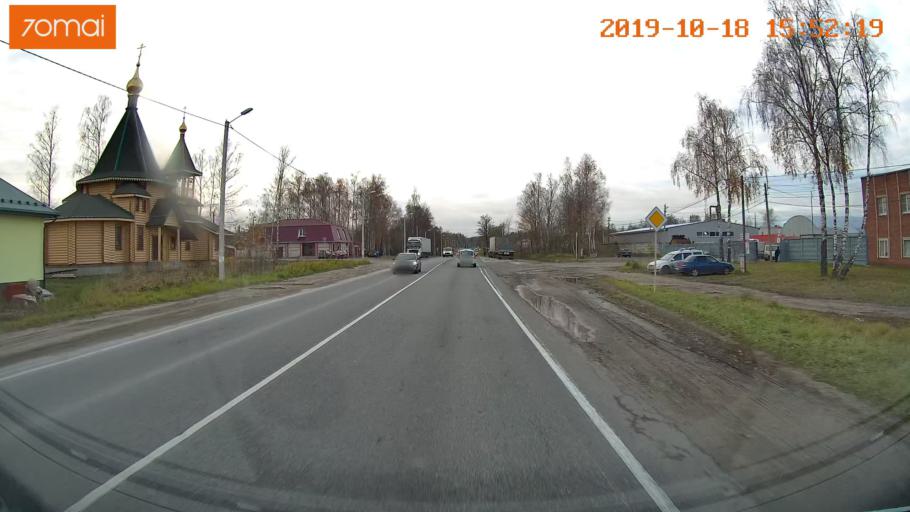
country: RU
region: Vladimir
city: Kommunar
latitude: 56.0472
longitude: 40.5361
